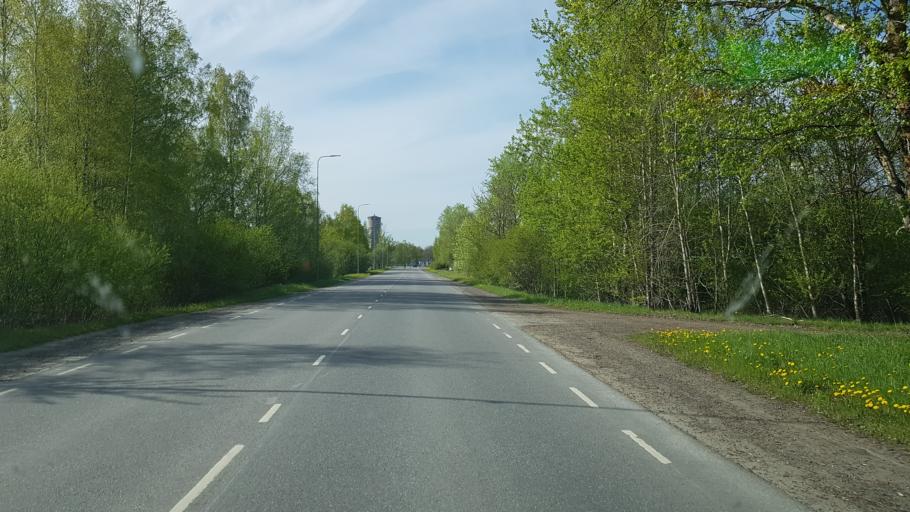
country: EE
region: Ida-Virumaa
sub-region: Kivioli linn
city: Kivioli
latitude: 59.3636
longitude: 26.9688
